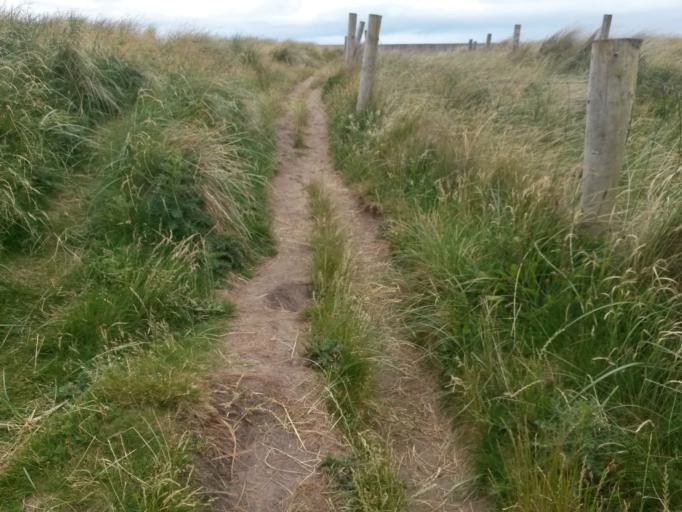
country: IE
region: Connaught
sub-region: Sligo
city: Strandhill
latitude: 54.2783
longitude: -8.6056
